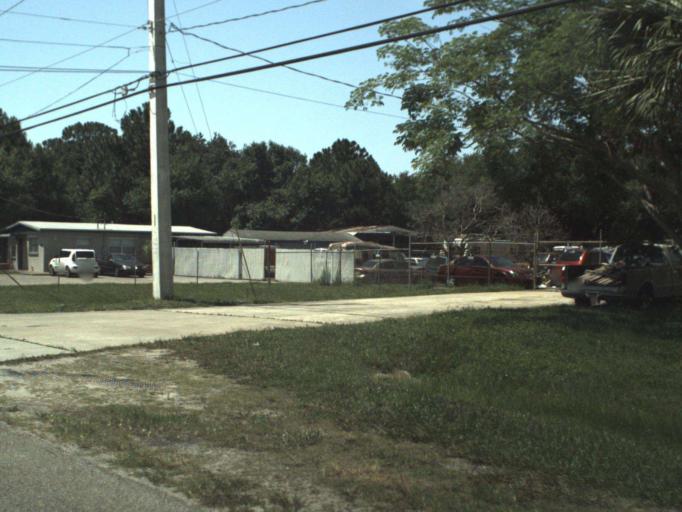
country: US
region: Florida
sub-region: Brevard County
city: Sharpes
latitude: 28.4315
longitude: -80.7081
